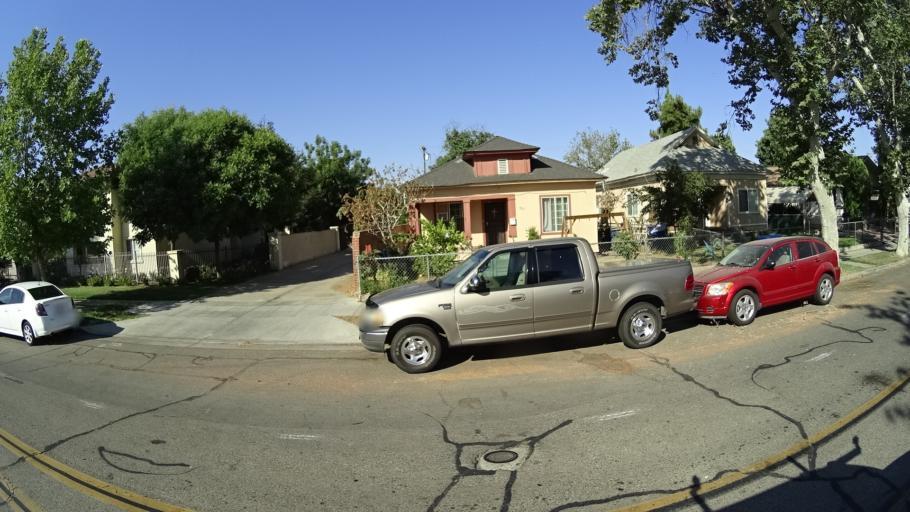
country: US
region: California
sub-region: Fresno County
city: Fresno
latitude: 36.7227
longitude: -119.7919
